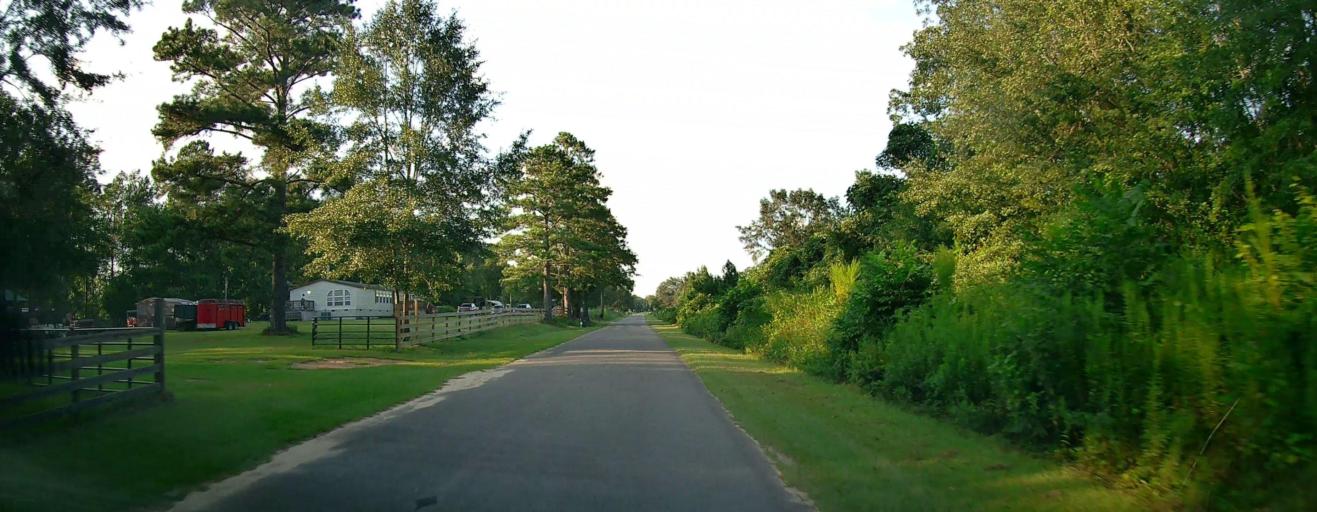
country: US
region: Georgia
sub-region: Crawford County
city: Roberta
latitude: 32.7061
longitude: -84.0088
